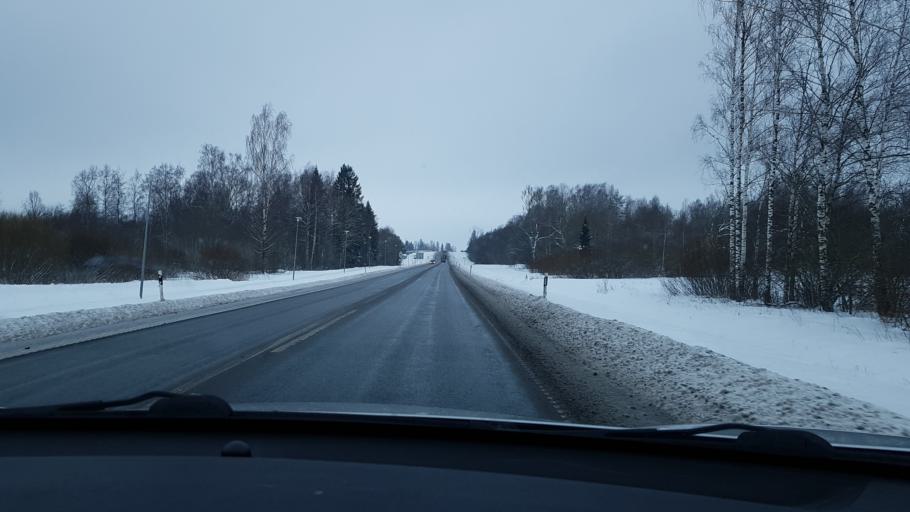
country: EE
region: Jaervamaa
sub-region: Tueri vald
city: Tueri
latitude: 58.8463
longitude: 25.4780
